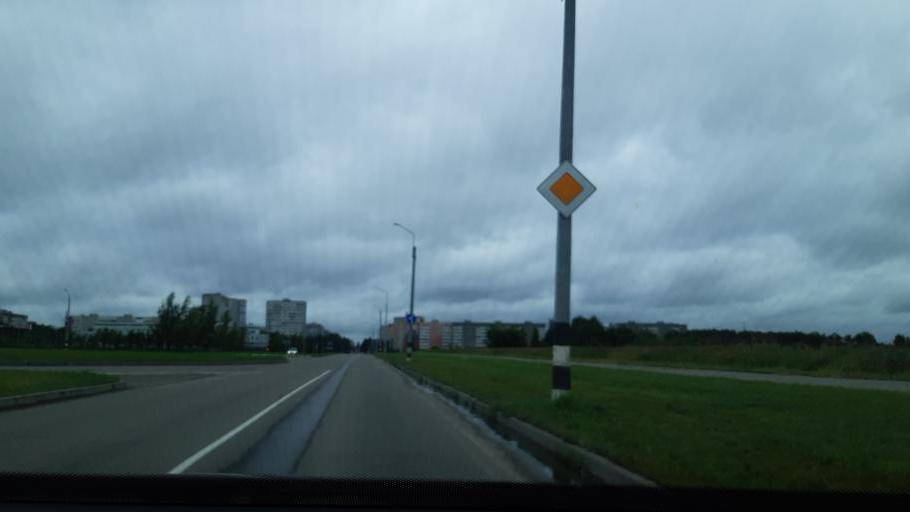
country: RU
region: Smolensk
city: Desnogorsk
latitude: 54.1424
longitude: 33.2796
